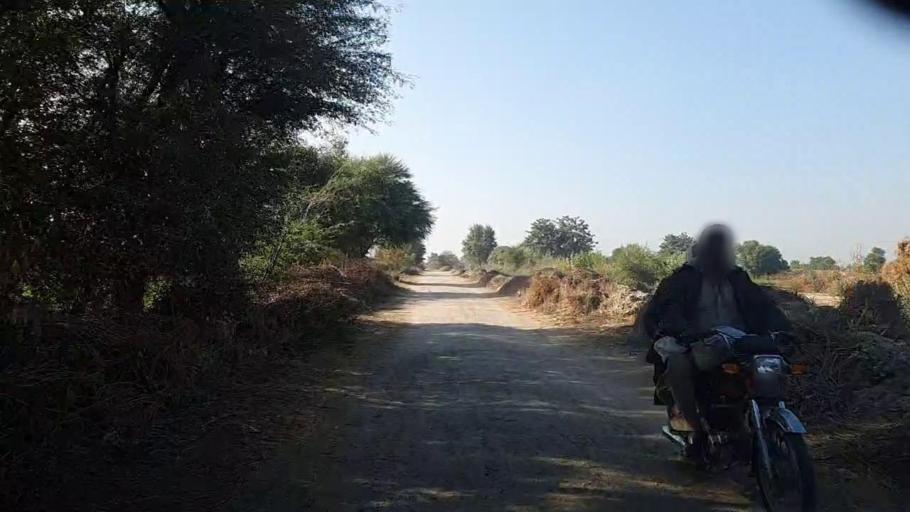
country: PK
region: Sindh
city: Darya Khan Marri
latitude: 26.6800
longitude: 68.3689
